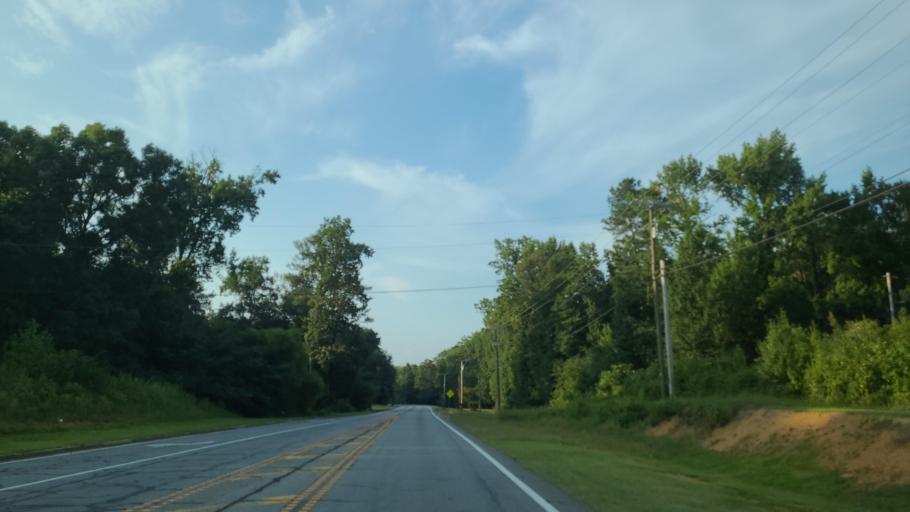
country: US
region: Georgia
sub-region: Whitfield County
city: Dalton
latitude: 34.6644
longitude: -84.9782
